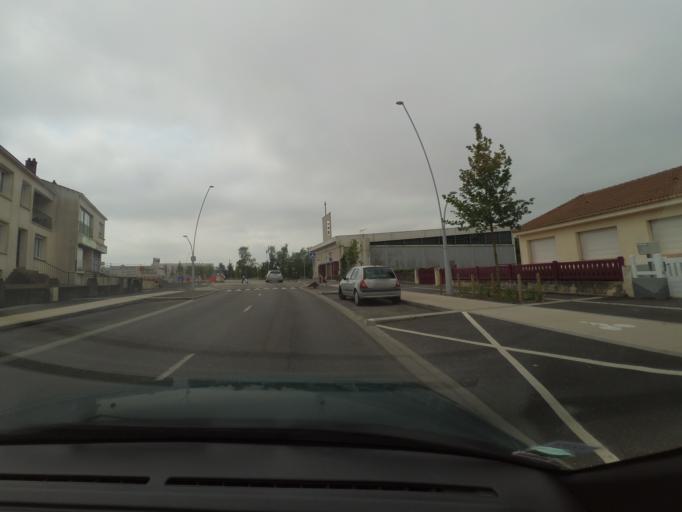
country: FR
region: Pays de la Loire
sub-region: Departement de la Vendee
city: La Roche-sur-Yon
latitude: 46.6803
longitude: -1.4407
